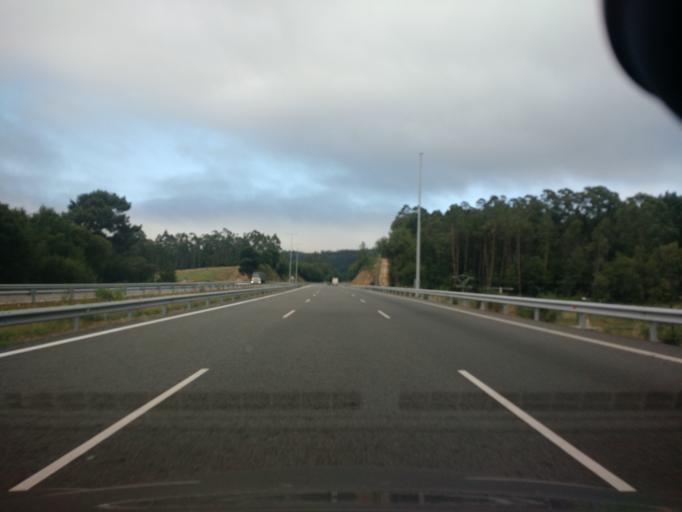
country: ES
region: Galicia
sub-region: Provincia da Coruna
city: Abegondo
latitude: 43.2013
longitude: -8.2964
